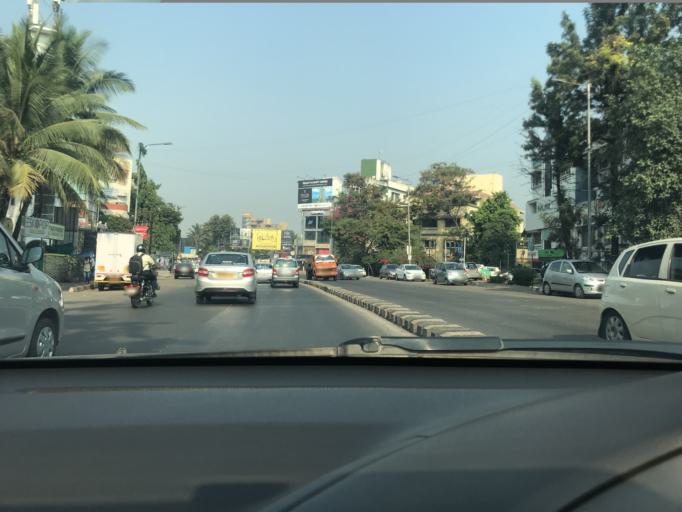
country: IN
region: Maharashtra
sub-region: Pune Division
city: Khadki
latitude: 18.5536
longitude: 73.8024
